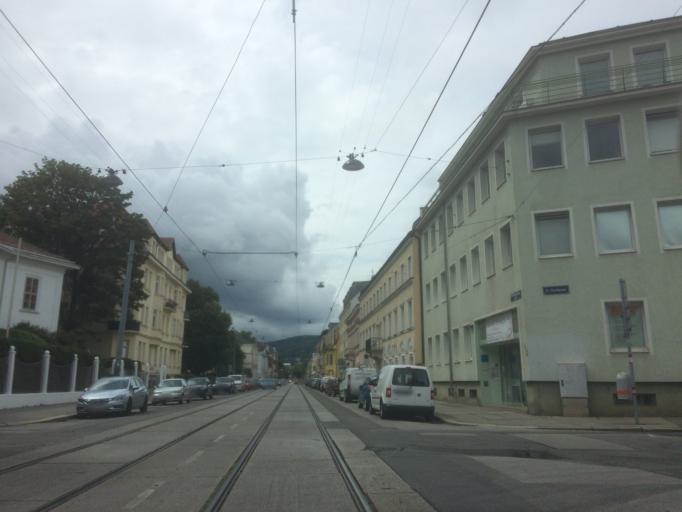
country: AT
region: Lower Austria
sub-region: Politischer Bezirk Modling
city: Perchtoldsdorf
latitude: 48.1872
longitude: 16.2880
